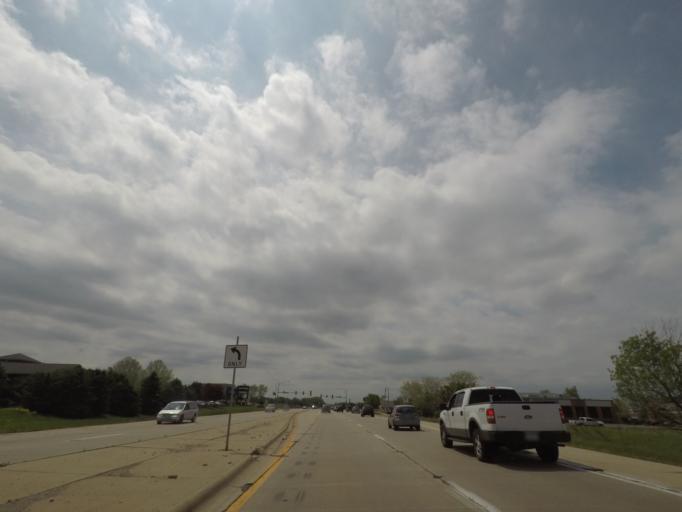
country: US
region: Illinois
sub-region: Winnebago County
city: Cherry Valley
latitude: 42.2986
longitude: -88.9801
